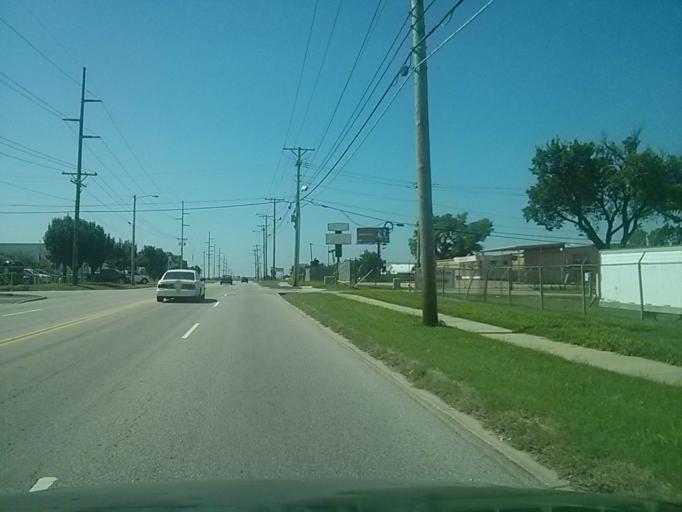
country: US
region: Oklahoma
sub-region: Tulsa County
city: Tulsa
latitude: 36.1448
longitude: -95.9047
